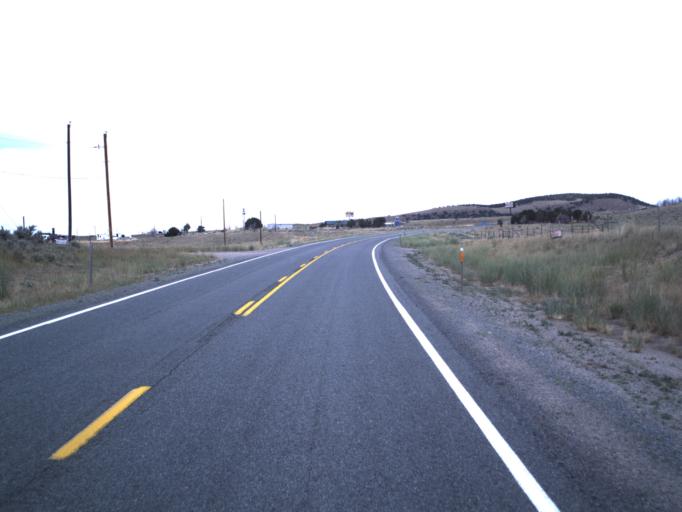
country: US
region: Utah
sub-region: Beaver County
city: Beaver
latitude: 38.6103
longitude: -112.5991
